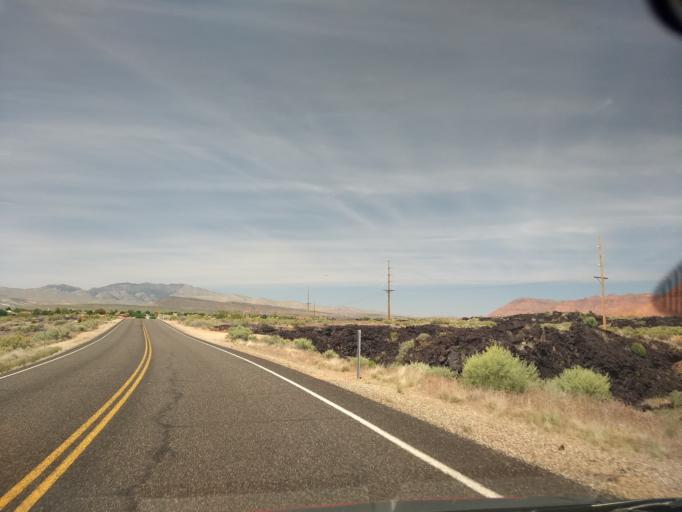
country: US
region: Utah
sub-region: Washington County
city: Santa Clara
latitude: 37.1440
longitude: -113.6471
